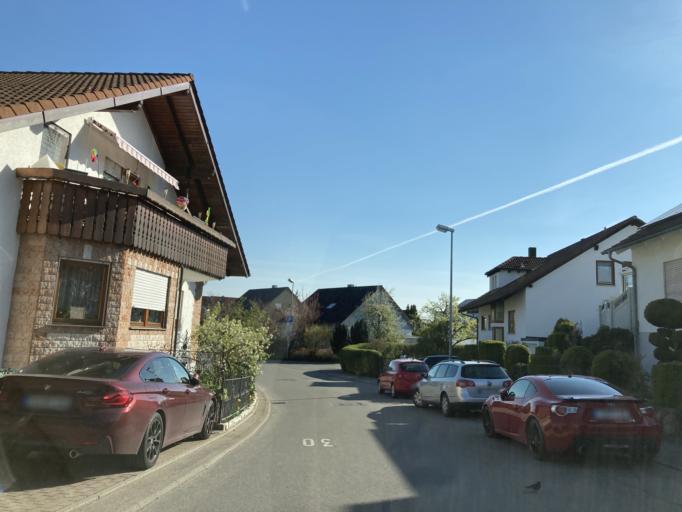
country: DE
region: Baden-Wuerttemberg
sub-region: Regierungsbezirk Stuttgart
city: Hildrizhausen
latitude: 48.5549
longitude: 8.9741
